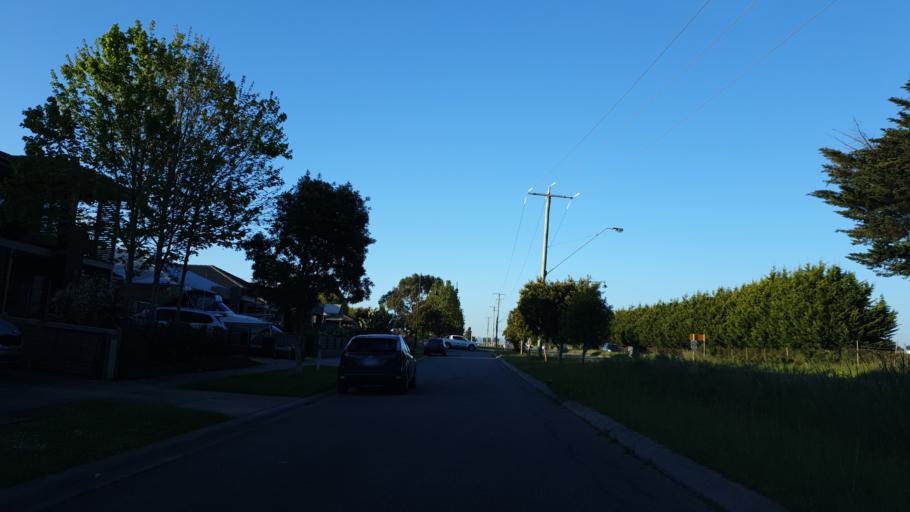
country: AU
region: Victoria
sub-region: Casey
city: Cranbourne
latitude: -38.0889
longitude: 145.2943
